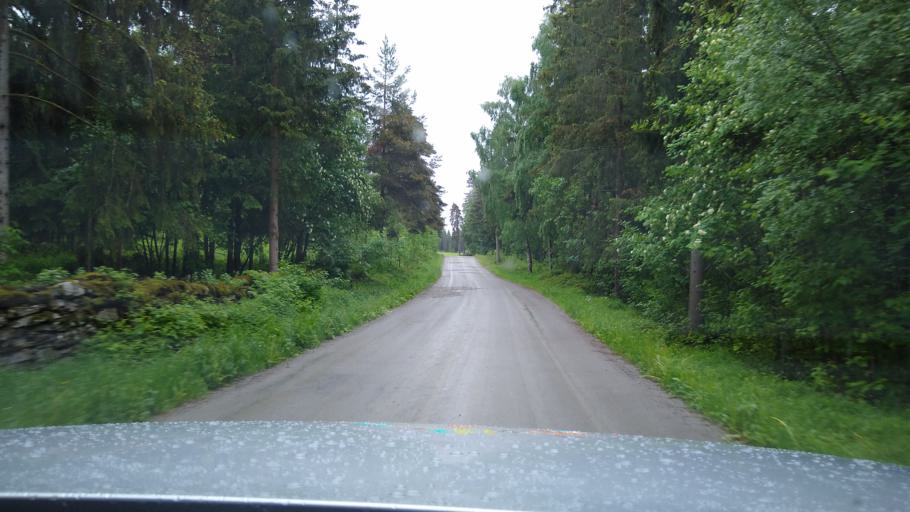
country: NO
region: Oppland
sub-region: Ringebu
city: Ringebu
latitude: 61.5414
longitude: 10.1126
